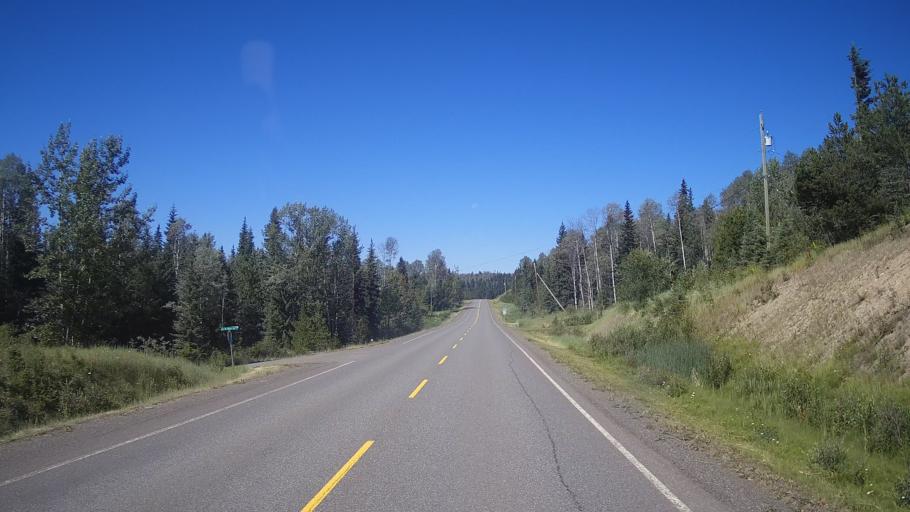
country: CA
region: British Columbia
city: Kamloops
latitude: 51.5043
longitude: -120.6154
